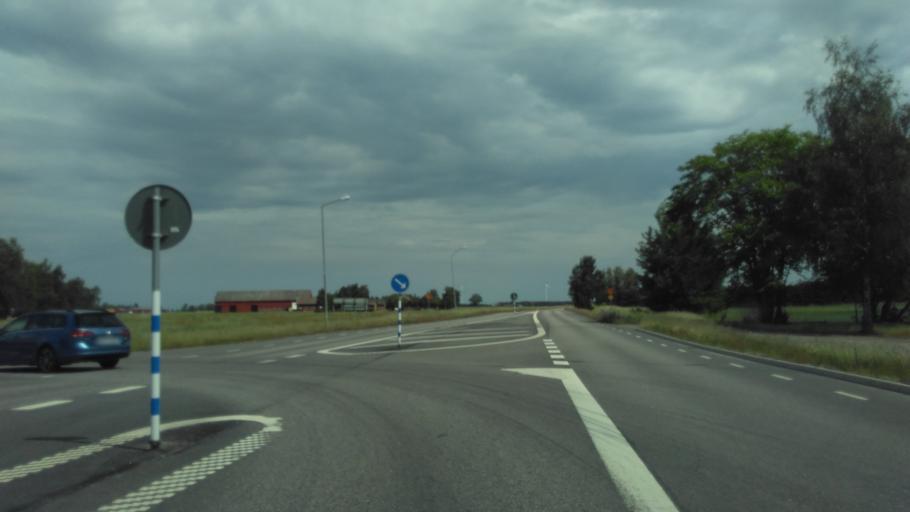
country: SE
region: Vaestra Goetaland
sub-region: Vara Kommun
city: Kvanum
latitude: 58.3334
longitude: 13.1242
